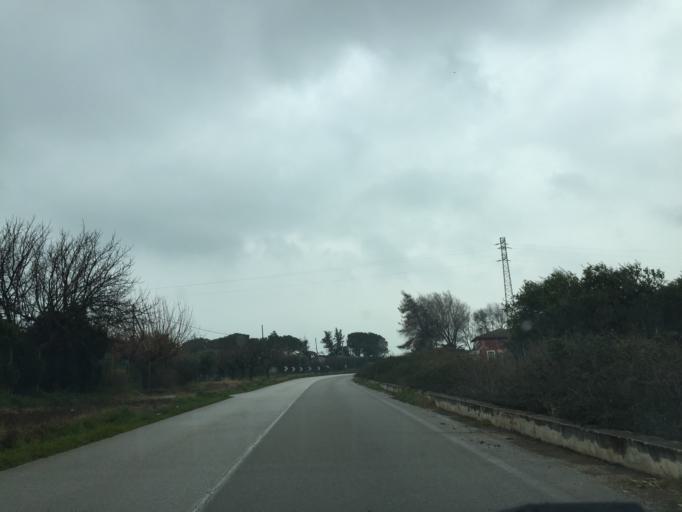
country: IT
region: Apulia
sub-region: Provincia di Foggia
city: Foggia
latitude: 41.4130
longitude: 15.4541
